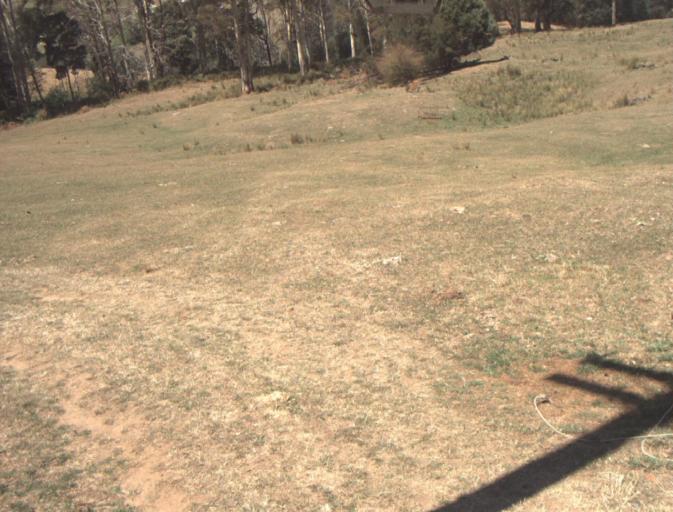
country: AU
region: Tasmania
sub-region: Launceston
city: Mayfield
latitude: -41.2687
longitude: 147.1219
